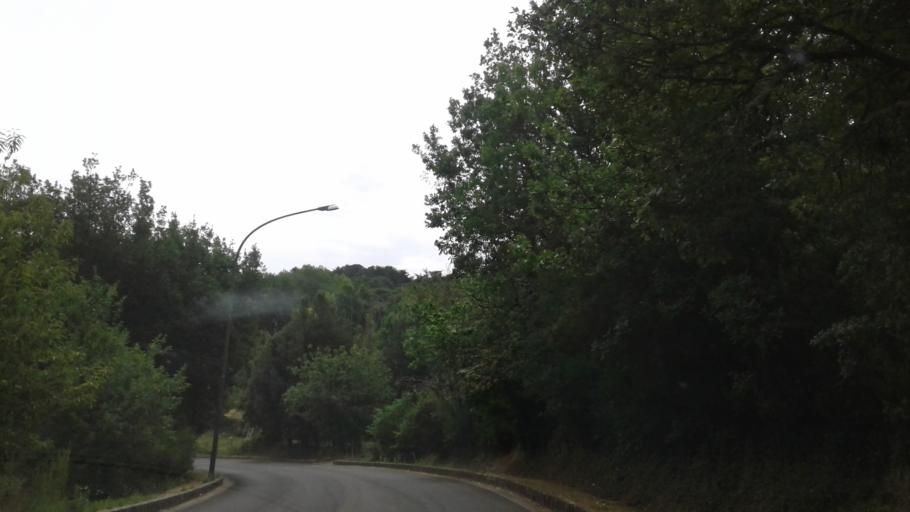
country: IT
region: Sardinia
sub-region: Provincia di Olbia-Tempio
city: Tempio Pausania
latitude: 40.9002
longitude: 9.0949
